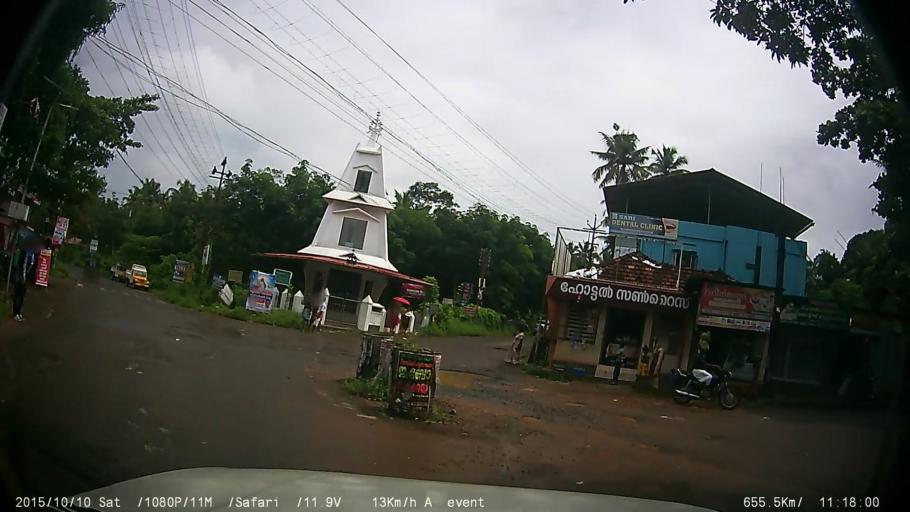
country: IN
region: Kerala
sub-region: Kottayam
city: Kottayam
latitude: 9.6421
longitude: 76.5336
